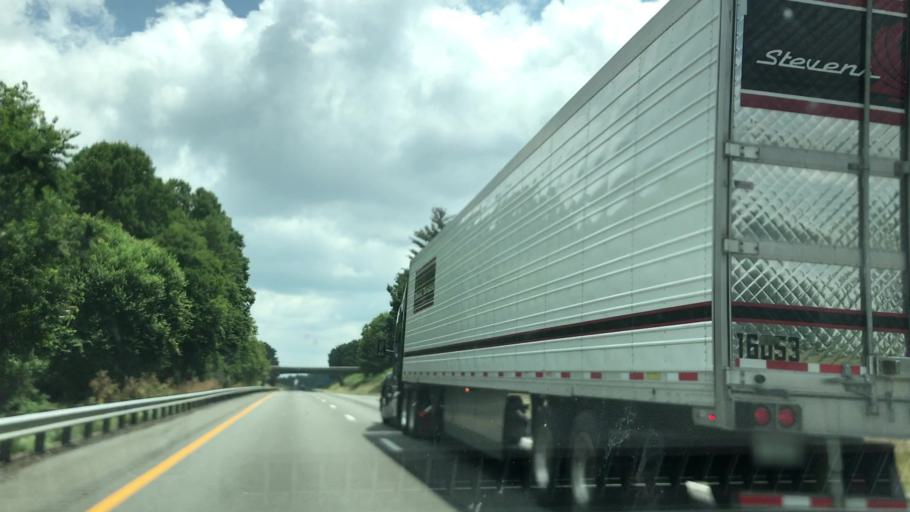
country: US
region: Virginia
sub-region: Carroll County
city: Woodlawn
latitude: 36.7704
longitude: -80.8073
